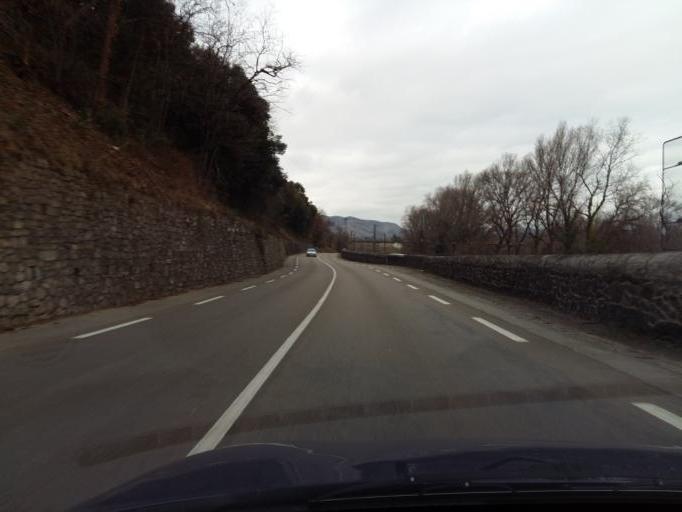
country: FR
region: Rhone-Alpes
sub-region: Departement de la Drome
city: La Roche-de-Glun
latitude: 45.0108
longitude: 4.8336
